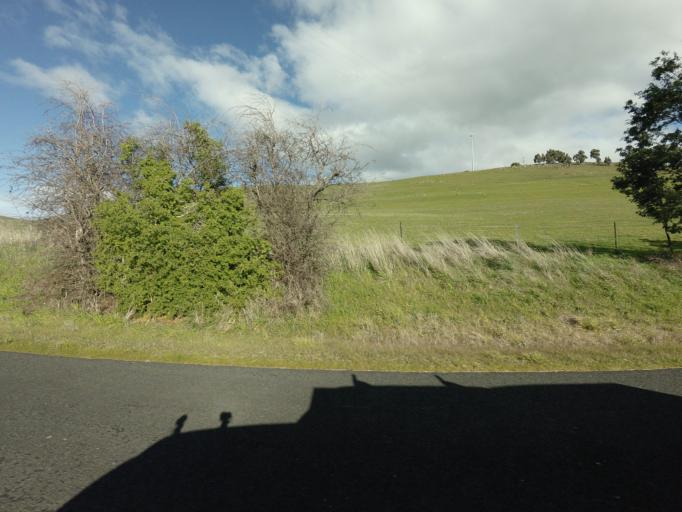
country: AU
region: Tasmania
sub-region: Derwent Valley
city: New Norfolk
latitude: -42.6931
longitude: 146.9473
